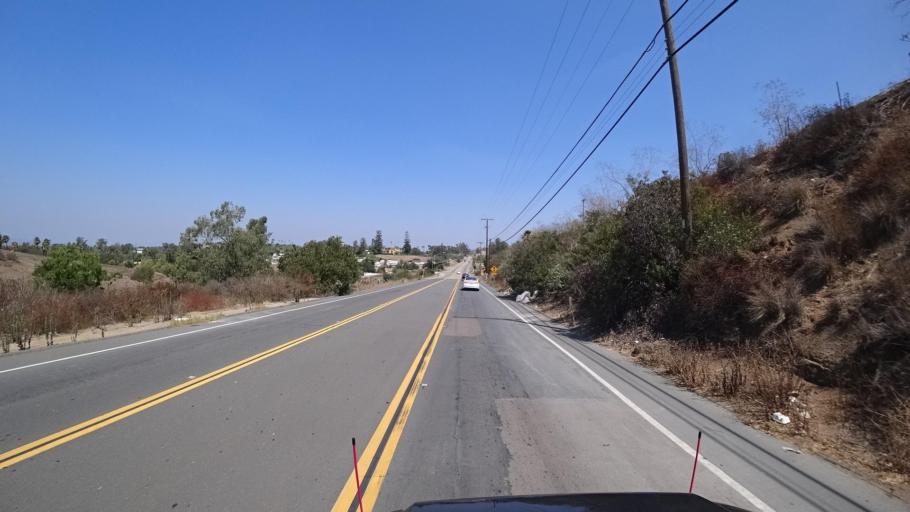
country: US
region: California
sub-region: San Diego County
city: Vista
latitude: 33.2359
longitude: -117.2263
